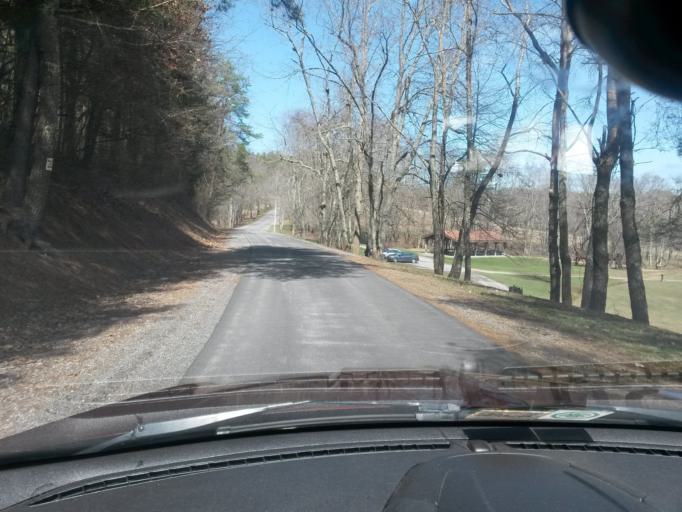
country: US
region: West Virginia
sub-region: Greenbrier County
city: Ronceverte
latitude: 37.6198
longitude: -80.3539
